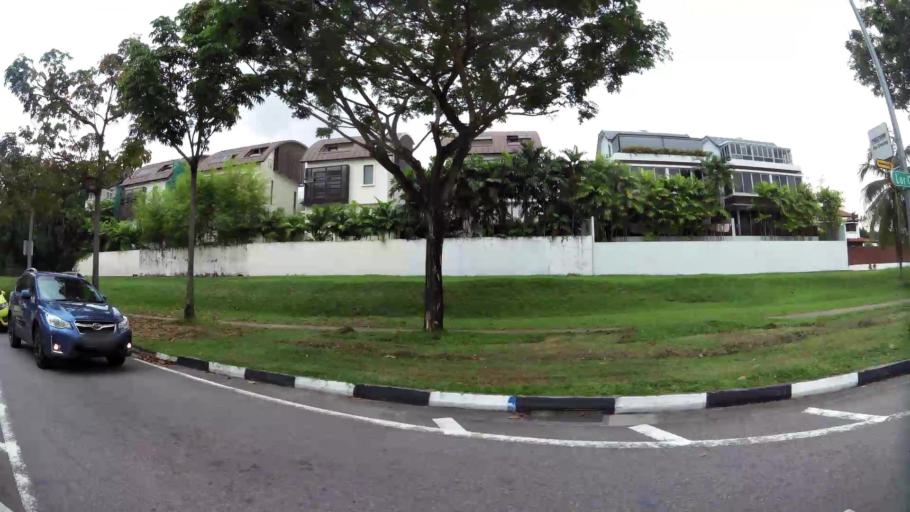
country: SG
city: Singapore
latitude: 1.3442
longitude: 103.8606
